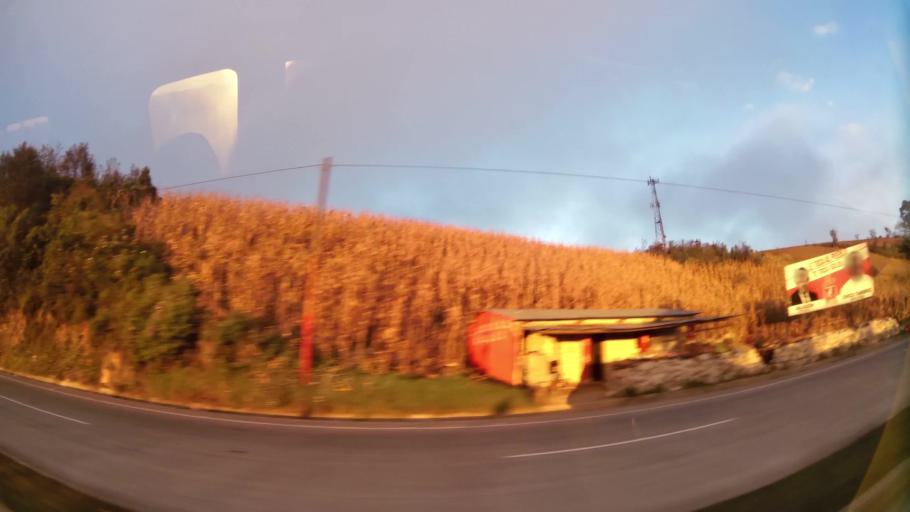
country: GT
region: Solola
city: Concepcion
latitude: 14.8367
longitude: -91.1272
